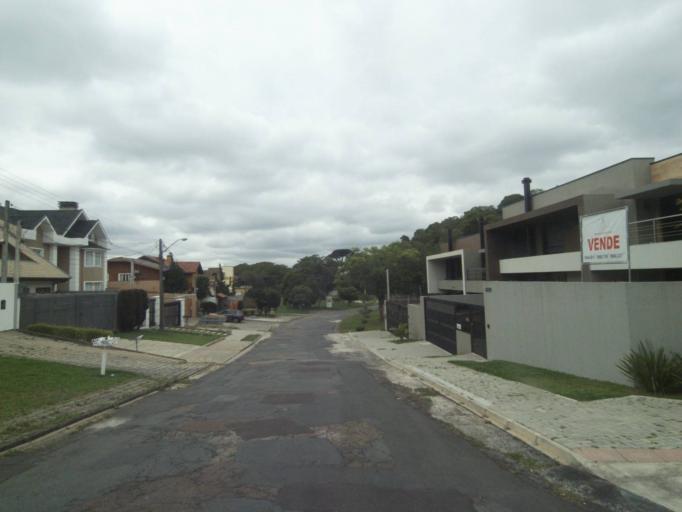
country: BR
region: Parana
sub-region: Curitiba
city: Curitiba
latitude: -25.3916
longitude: -49.2758
